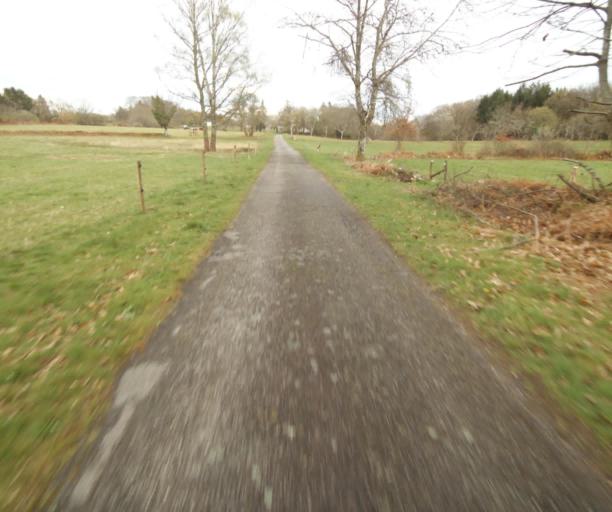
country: FR
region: Limousin
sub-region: Departement de la Correze
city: Saint-Privat
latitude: 45.2191
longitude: 2.0144
